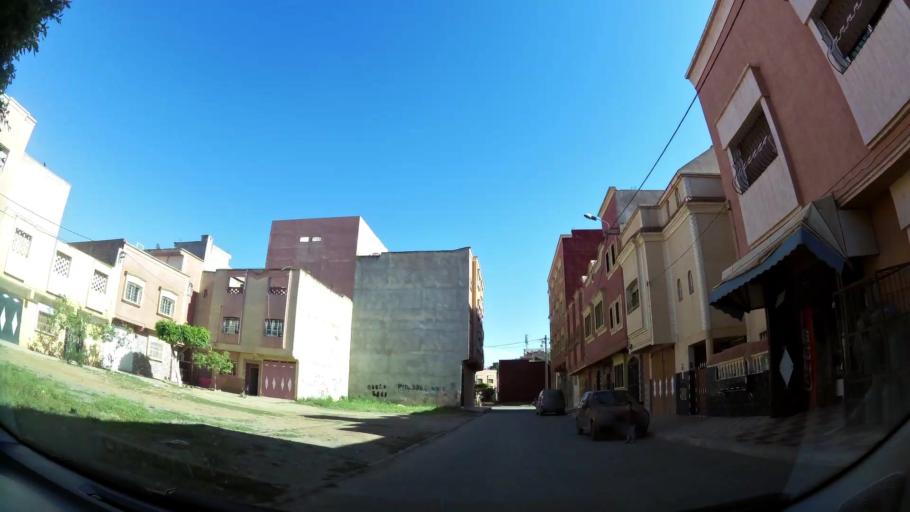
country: MA
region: Oriental
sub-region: Berkane-Taourirt
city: Berkane
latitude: 34.9370
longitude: -2.3365
